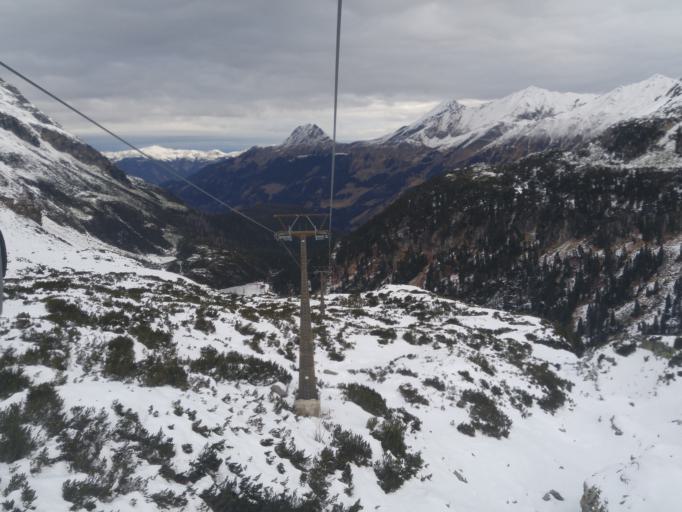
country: AT
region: Salzburg
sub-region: Politischer Bezirk Zell am See
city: Niedernsill
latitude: 47.1477
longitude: 12.6247
